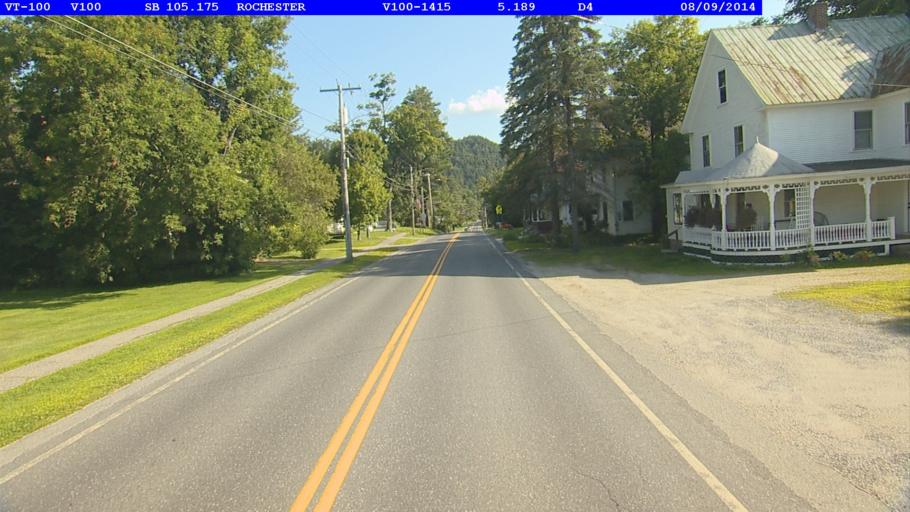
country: US
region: Vermont
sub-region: Orange County
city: Randolph
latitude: 43.8731
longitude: -72.8082
